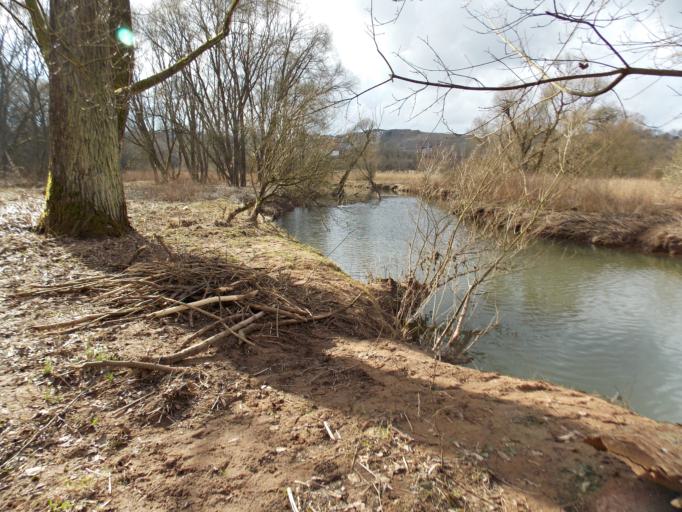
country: DE
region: Saarland
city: Neunkirchen
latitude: 49.3635
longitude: 7.1753
